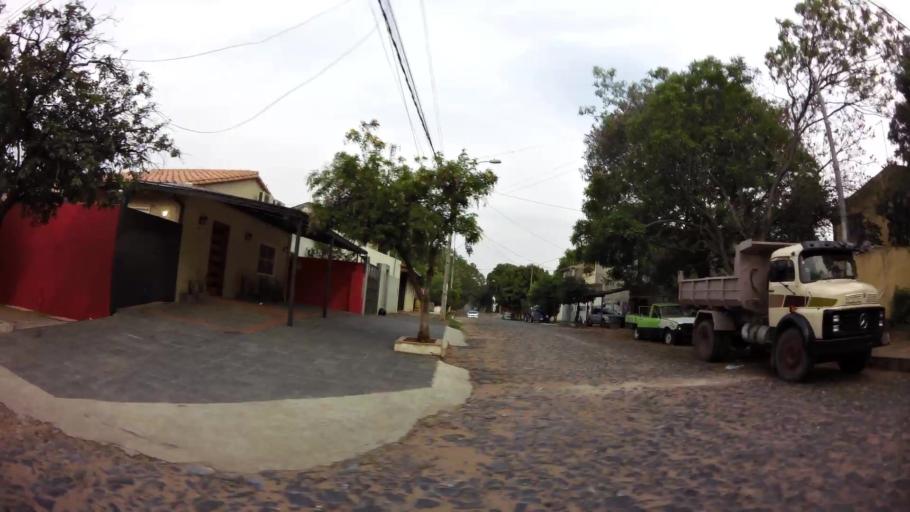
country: PY
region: Asuncion
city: Asuncion
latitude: -25.2990
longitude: -57.6102
